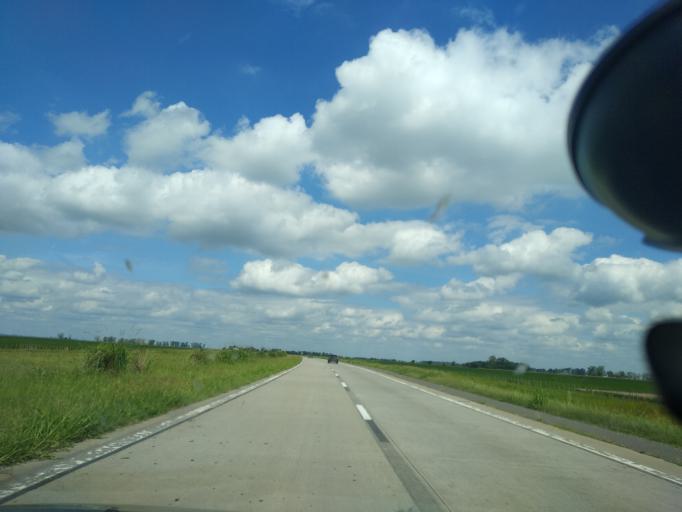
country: AR
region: Cordoba
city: General Roca
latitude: -32.6862
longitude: -62.0042
